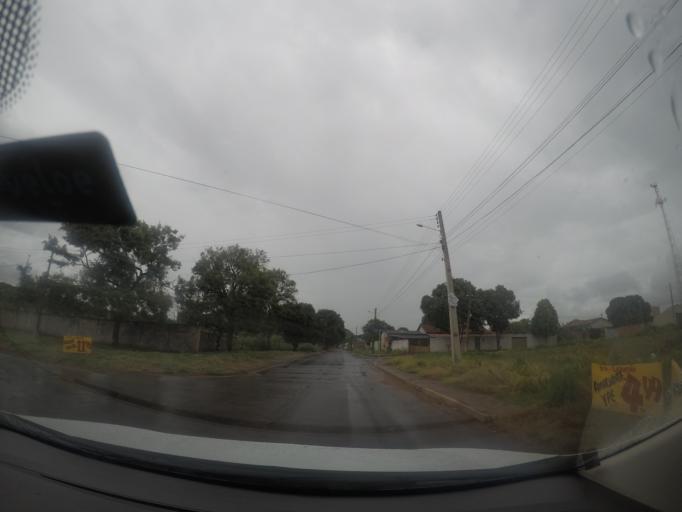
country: BR
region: Goias
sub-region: Trindade
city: Trindade
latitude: -16.6410
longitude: -49.4306
